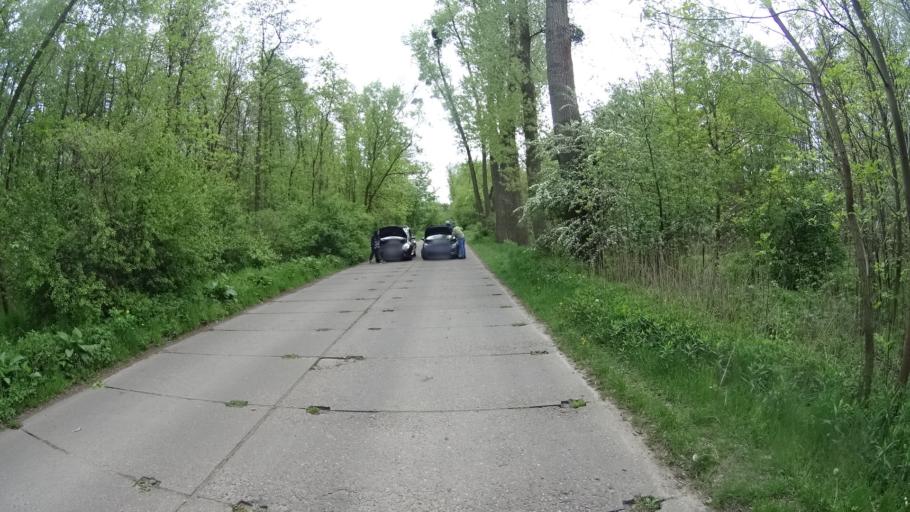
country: PL
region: Masovian Voivodeship
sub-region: Warszawa
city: Bemowo
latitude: 52.2830
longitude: 20.8866
